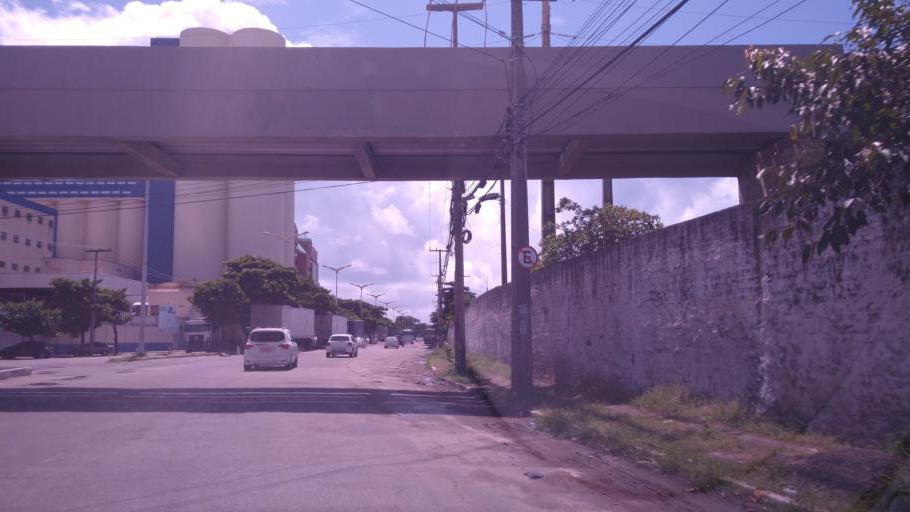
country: BR
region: Ceara
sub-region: Fortaleza
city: Fortaleza
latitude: -3.7168
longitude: -38.4751
